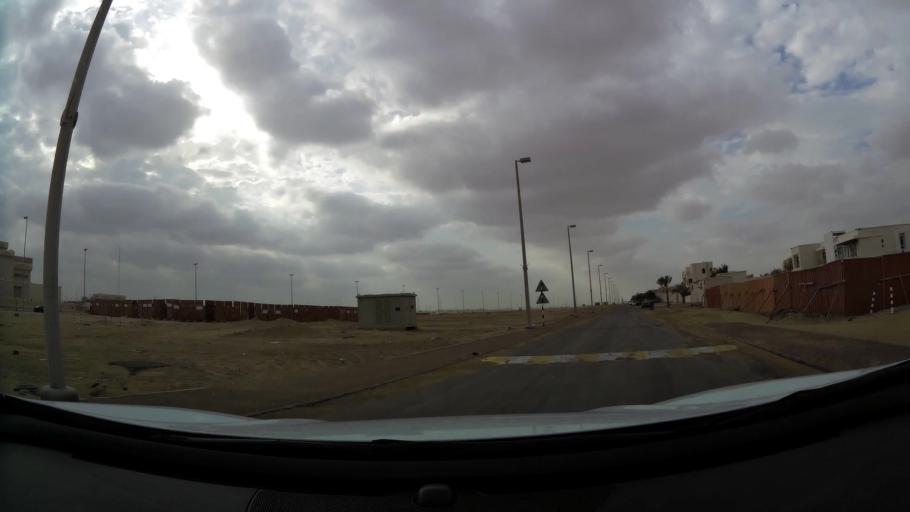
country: AE
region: Abu Dhabi
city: Abu Dhabi
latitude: 24.3428
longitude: 54.6159
